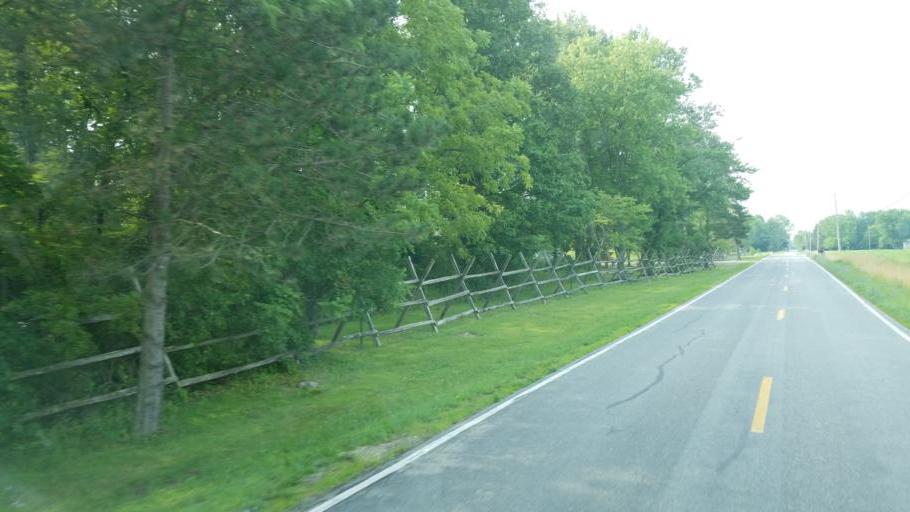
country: US
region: Ohio
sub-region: Union County
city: New California
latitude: 40.2073
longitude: -83.1663
